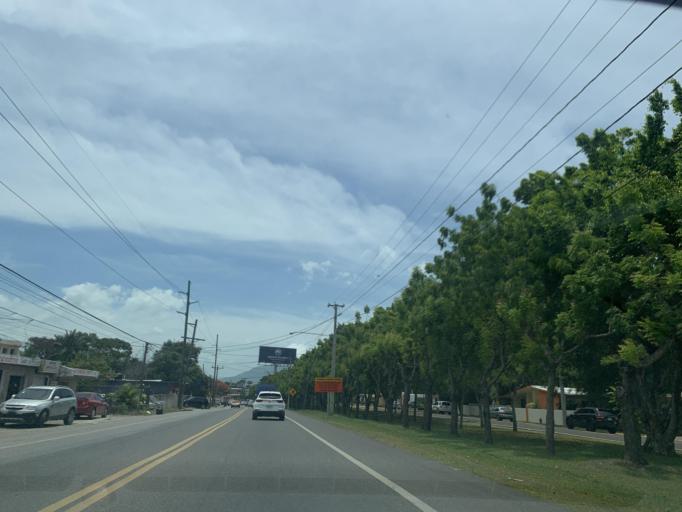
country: DO
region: Puerto Plata
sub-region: Puerto Plata
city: Puerto Plata
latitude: 19.7505
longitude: -70.5783
